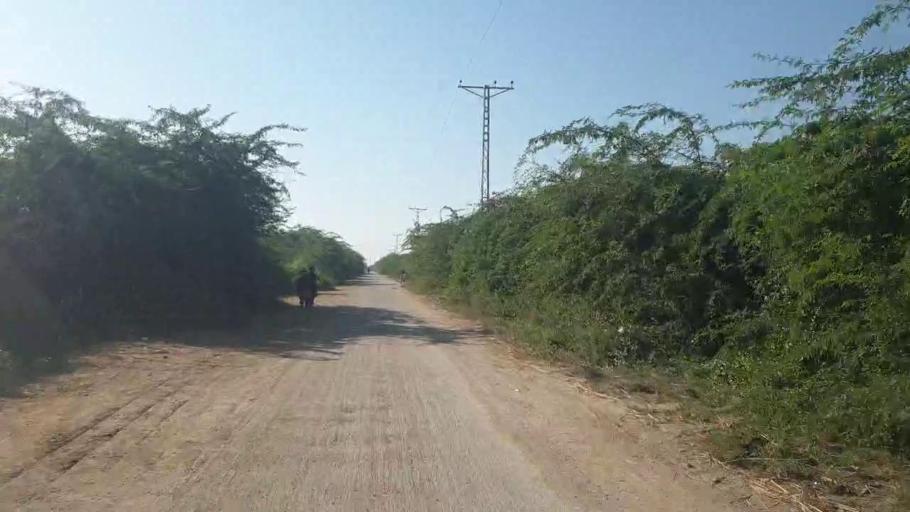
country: PK
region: Sindh
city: Rajo Khanani
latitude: 24.9497
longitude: 68.7941
